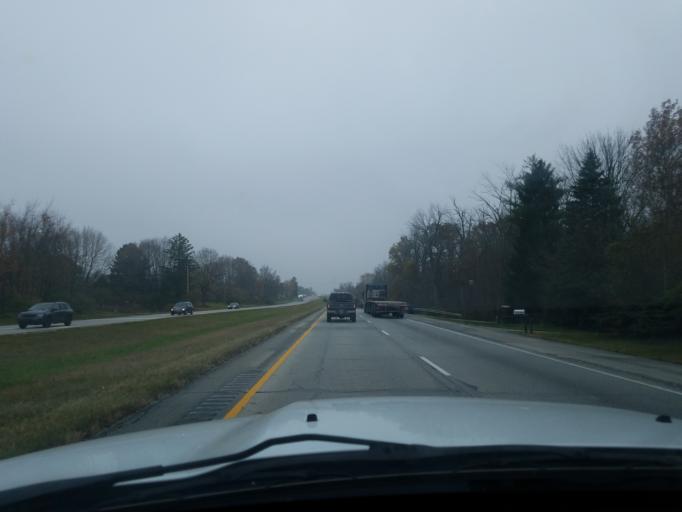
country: US
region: Indiana
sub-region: Hamilton County
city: Westfield
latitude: 40.1350
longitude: -86.1279
